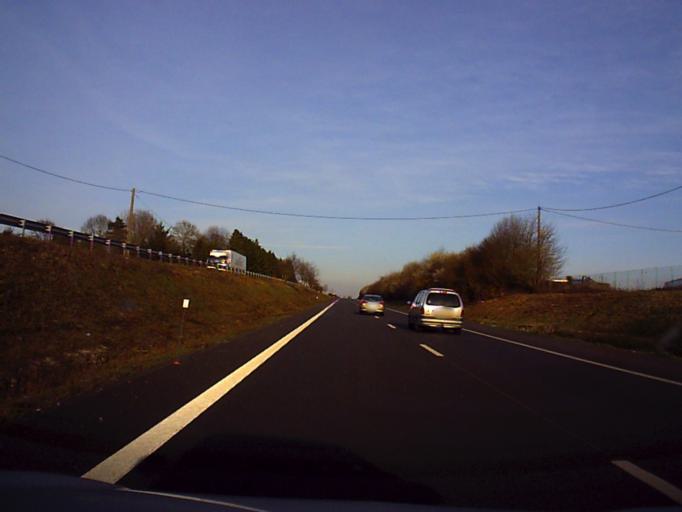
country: FR
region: Brittany
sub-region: Departement d'Ille-et-Vilaine
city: Monterfil
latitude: 48.0330
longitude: -1.9869
